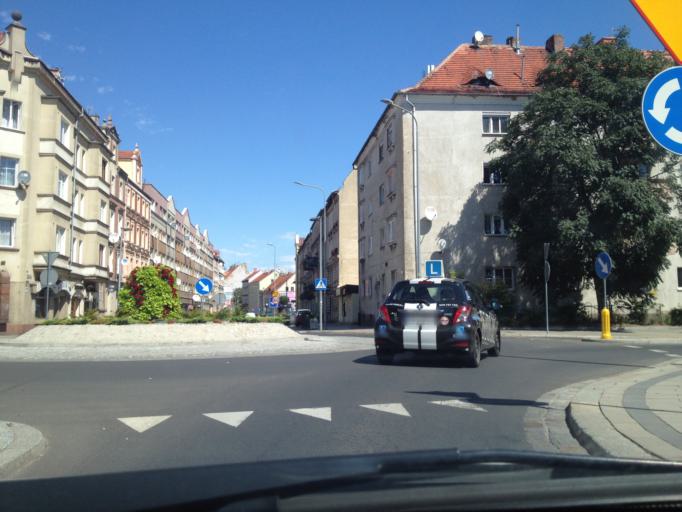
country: PL
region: Lower Silesian Voivodeship
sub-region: Legnica
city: Legnica
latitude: 51.2002
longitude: 16.1595
